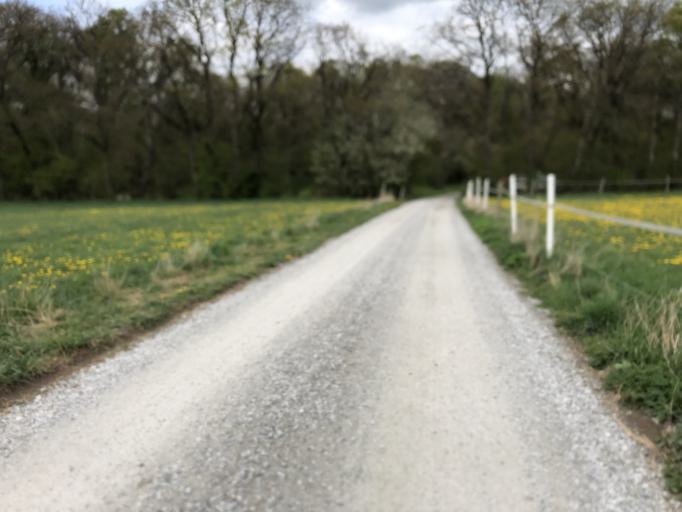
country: SE
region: Skane
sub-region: Eslovs Kommun
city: Eslov
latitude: 55.7317
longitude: 13.2991
